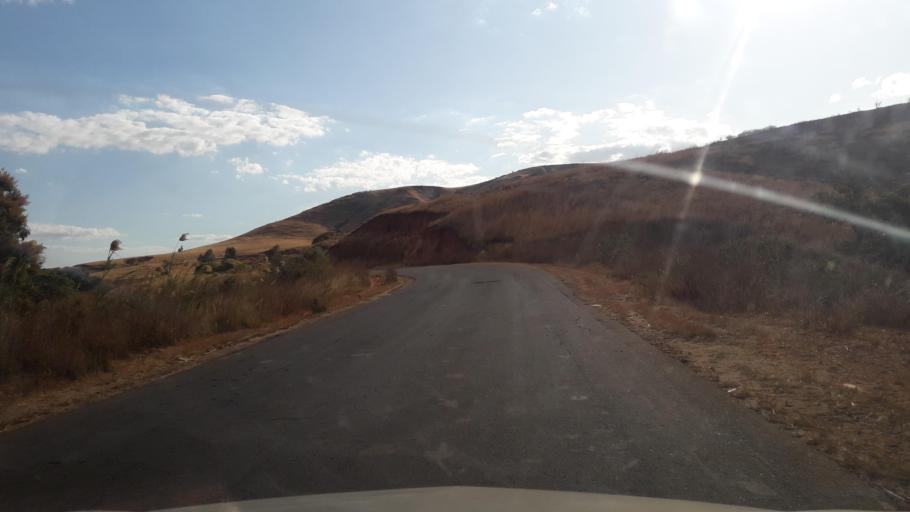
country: MG
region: Betsiboka
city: Maevatanana
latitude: -17.4807
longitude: 46.9941
